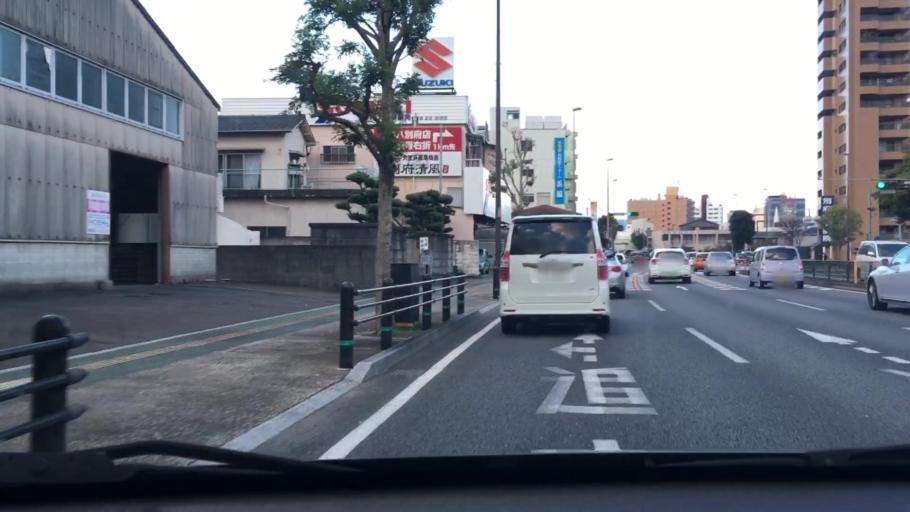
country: JP
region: Oita
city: Beppu
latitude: 33.2693
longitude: 131.5100
